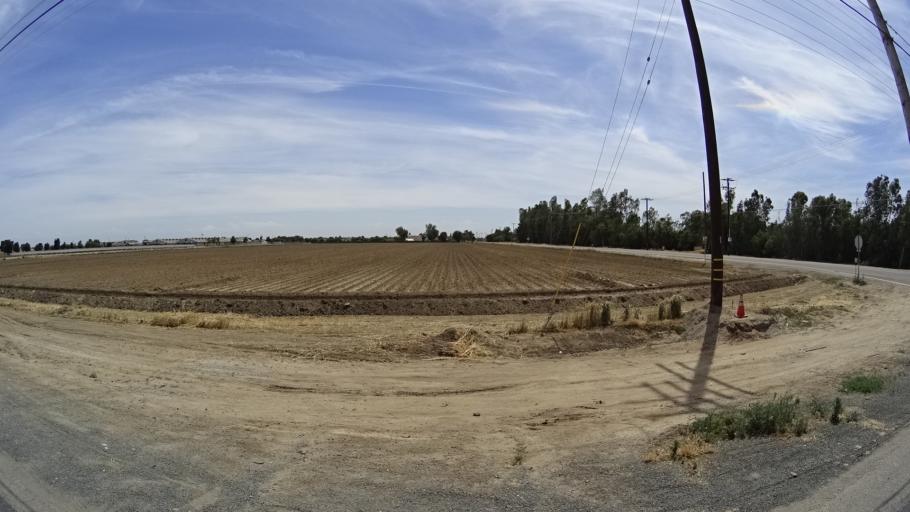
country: US
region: California
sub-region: Kings County
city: Armona
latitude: 36.3429
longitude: -119.6910
